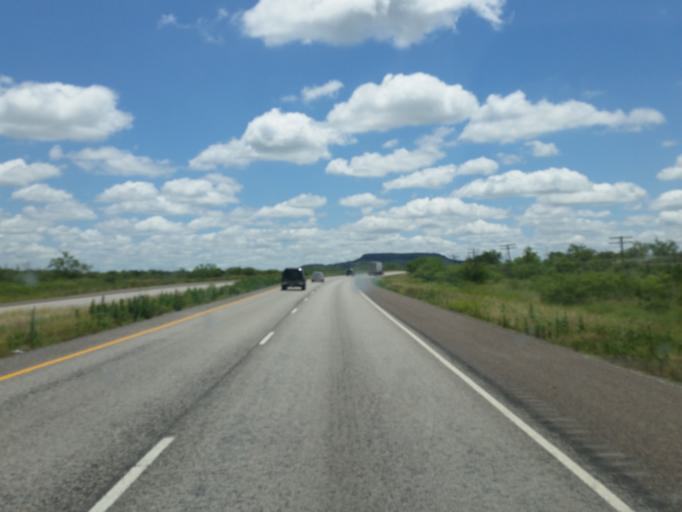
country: US
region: Texas
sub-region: Scurry County
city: Snyder
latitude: 32.9802
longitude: -101.1089
